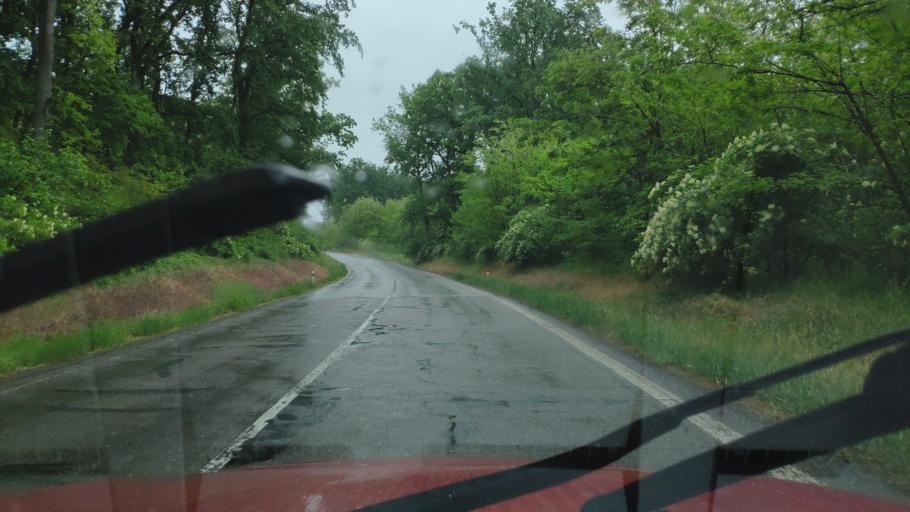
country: HU
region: Borsod-Abauj-Zemplen
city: Ricse
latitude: 48.4376
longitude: 21.9473
